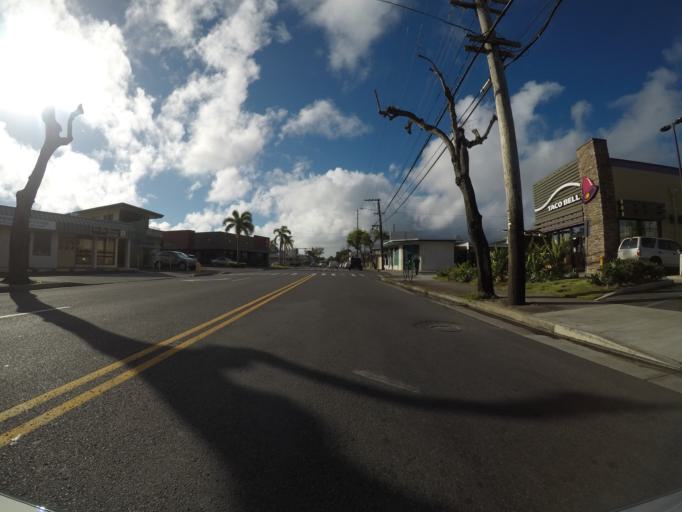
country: US
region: Hawaii
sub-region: Honolulu County
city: Kailua
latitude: 21.3965
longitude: -157.7456
